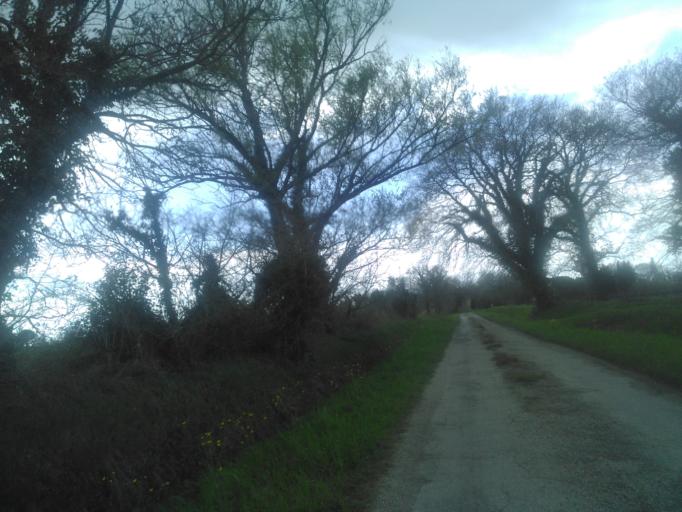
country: FR
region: Provence-Alpes-Cote d'Azur
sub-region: Departement des Bouches-du-Rhone
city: Arles
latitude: 43.6359
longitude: 4.5825
